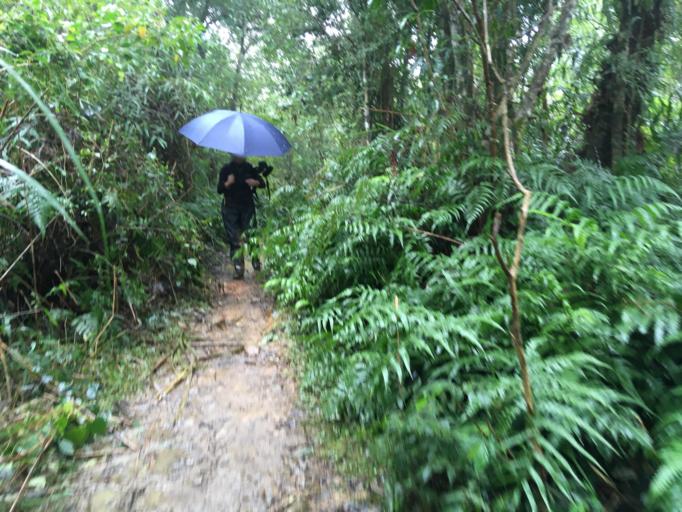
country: TW
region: Taiwan
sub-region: Yilan
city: Yilan
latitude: 24.6773
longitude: 121.5704
